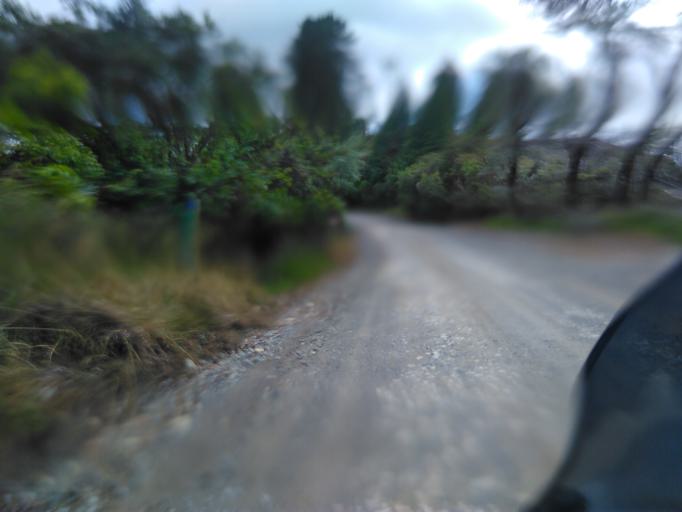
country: NZ
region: Gisborne
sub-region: Gisborne District
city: Gisborne
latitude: -38.2386
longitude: 178.0702
